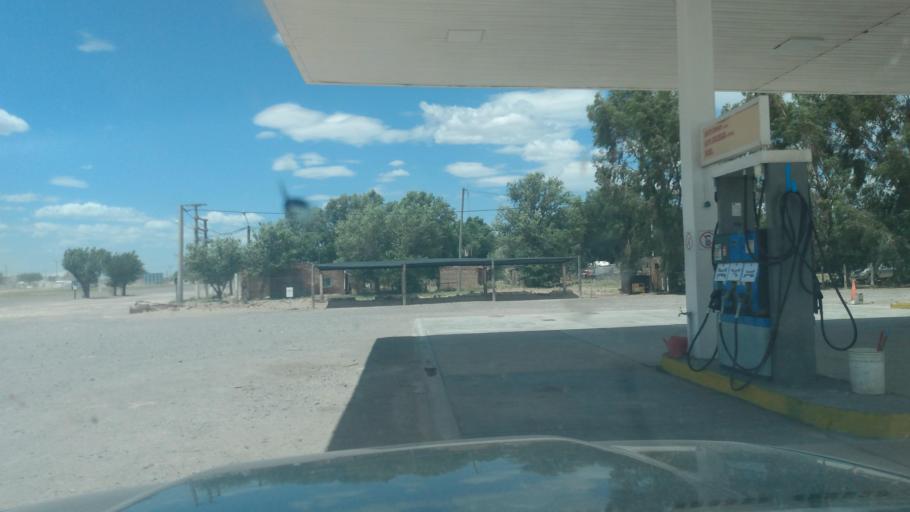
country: AR
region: La Pampa
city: Puelches
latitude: -38.1442
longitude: -65.9171
